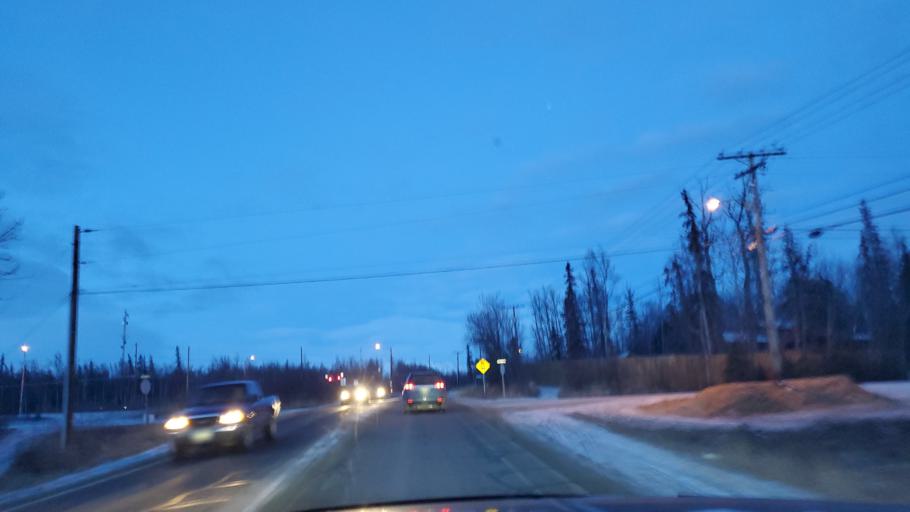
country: US
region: Alaska
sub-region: Matanuska-Susitna Borough
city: Lakes
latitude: 61.5971
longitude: -149.3598
